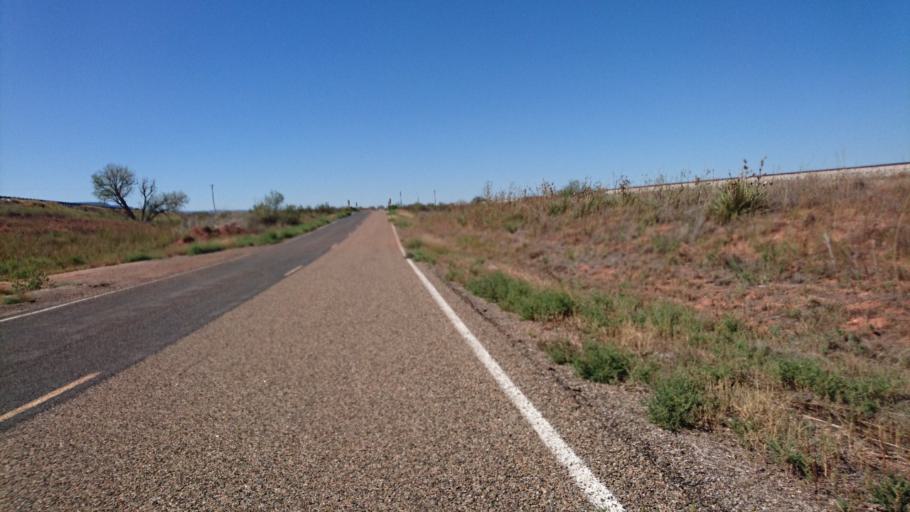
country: US
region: New Mexico
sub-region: Quay County
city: Tucumcari
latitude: 35.1000
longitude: -104.0506
